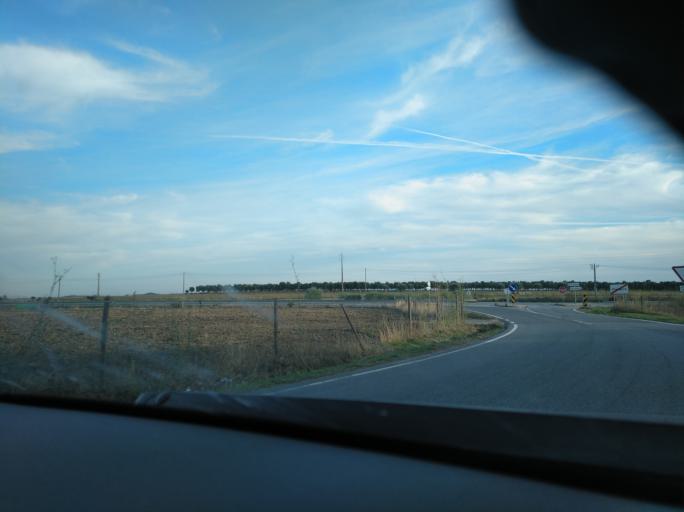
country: PT
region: Evora
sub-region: Arraiolos
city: Arraiolos
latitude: 38.8277
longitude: -7.8425
